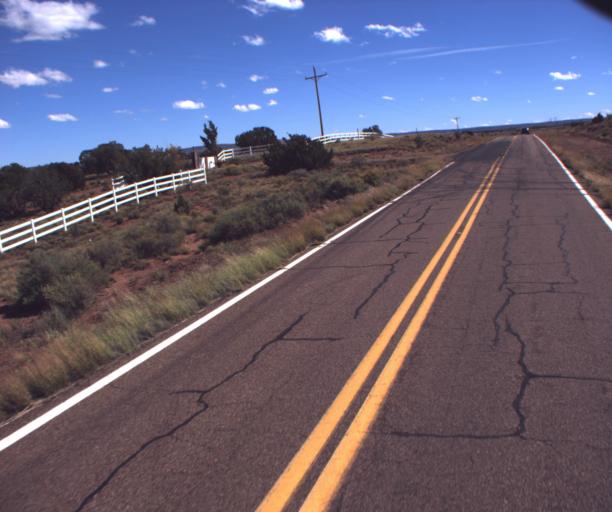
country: US
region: Arizona
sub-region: Apache County
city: Saint Johns
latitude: 34.5833
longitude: -109.6421
